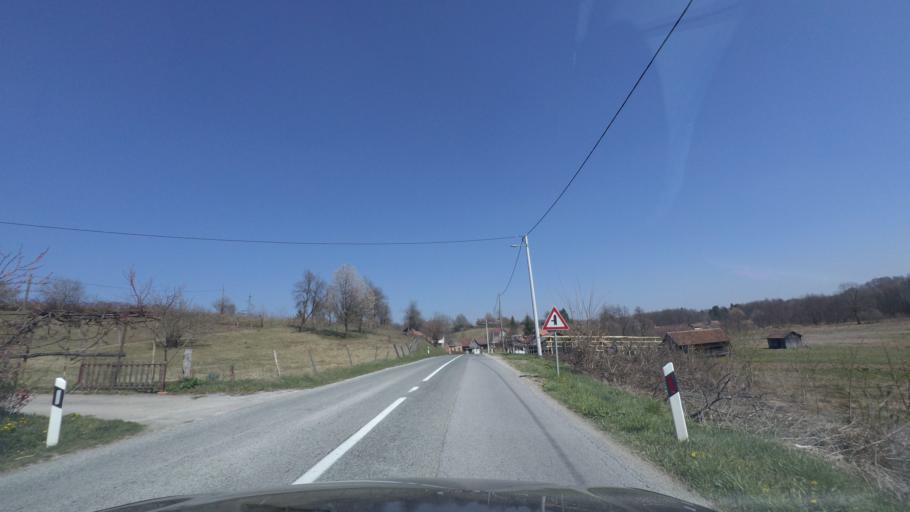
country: HR
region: Karlovacka
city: Vojnic
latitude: 45.3372
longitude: 15.7212
